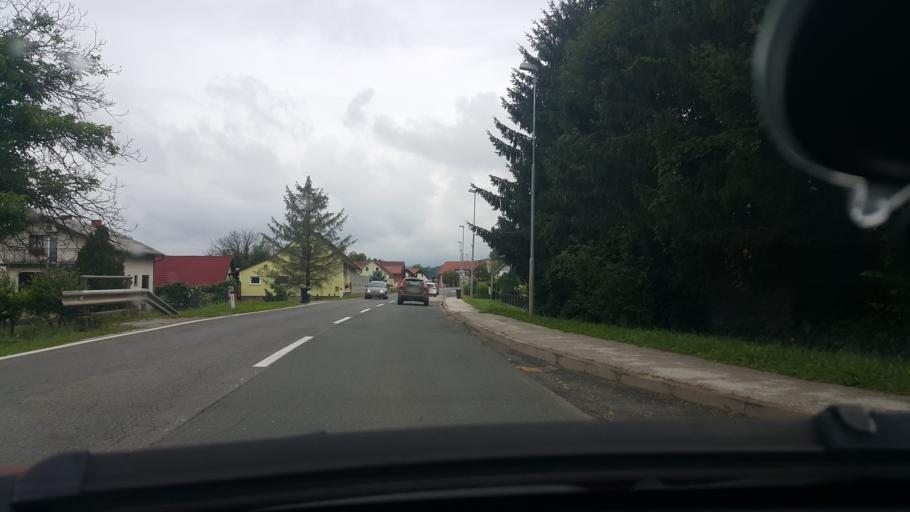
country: SI
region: Ormoz
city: Ormoz
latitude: 46.4148
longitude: 16.1134
